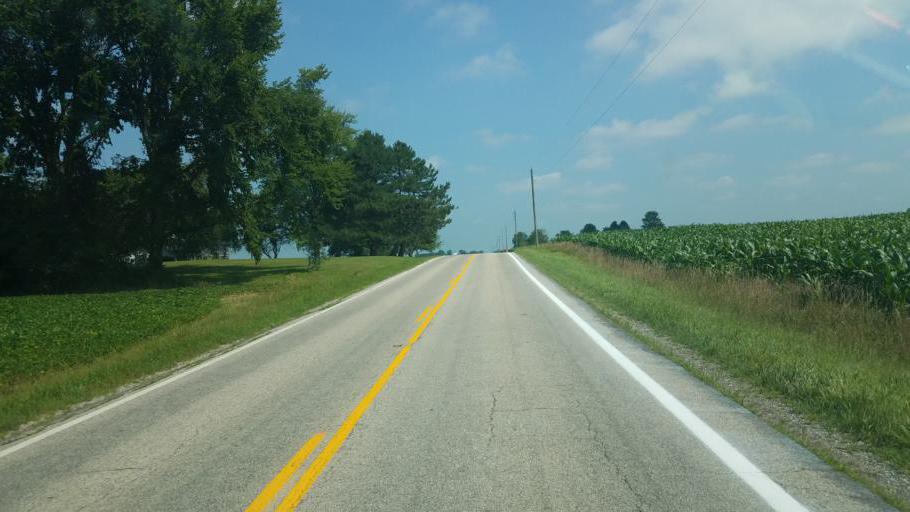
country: US
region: Ohio
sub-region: Crawford County
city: Bucyrus
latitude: 40.9050
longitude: -82.8546
